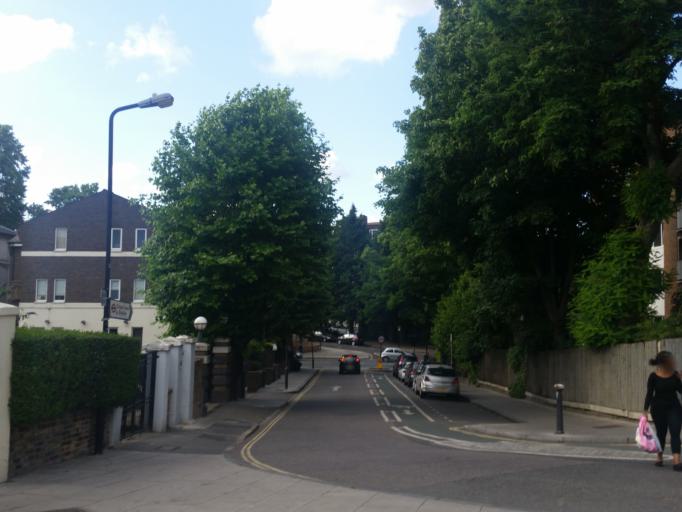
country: GB
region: England
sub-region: Greater London
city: Camden Town
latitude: 51.5433
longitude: -0.1548
